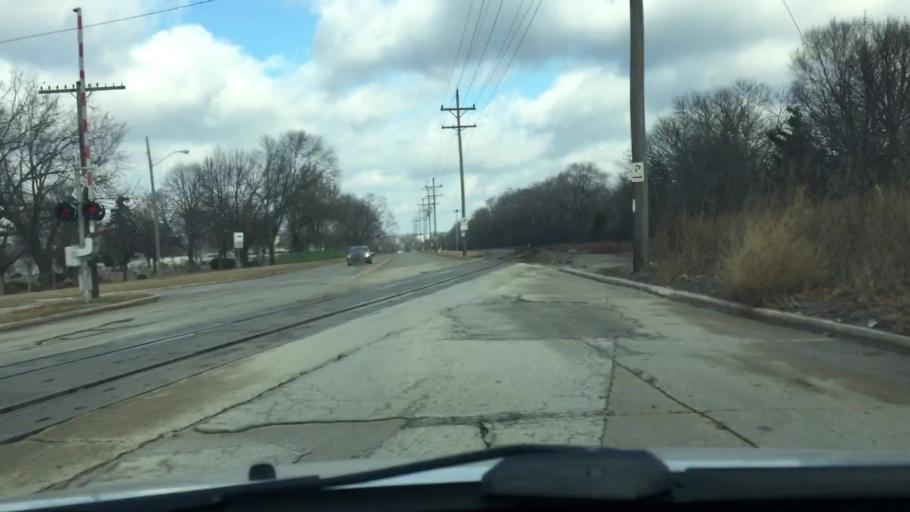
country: US
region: Wisconsin
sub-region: Waukesha County
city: Waukesha
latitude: 42.9937
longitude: -88.2369
